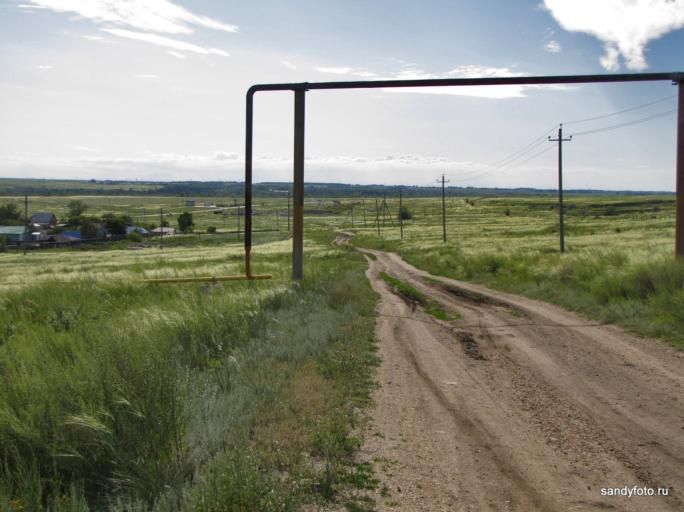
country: RU
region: Chelyabinsk
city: Troitsk
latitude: 54.1007
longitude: 61.5442
